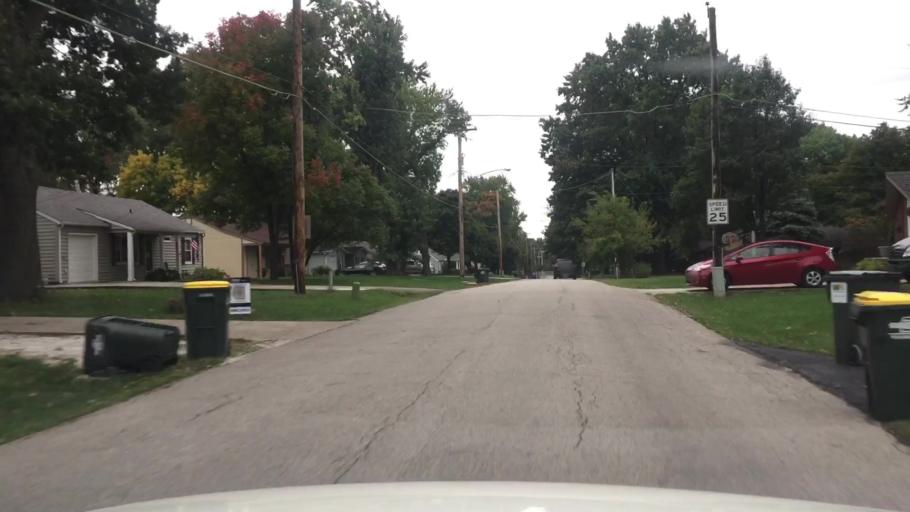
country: US
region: Kansas
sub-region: Johnson County
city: Shawnee
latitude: 39.0331
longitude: -94.7286
